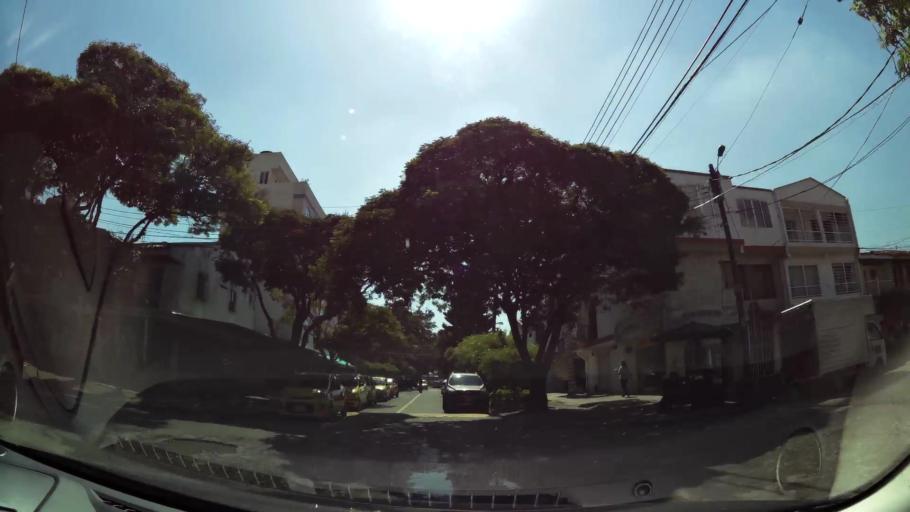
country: CO
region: Valle del Cauca
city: Cali
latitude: 3.4275
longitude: -76.5307
